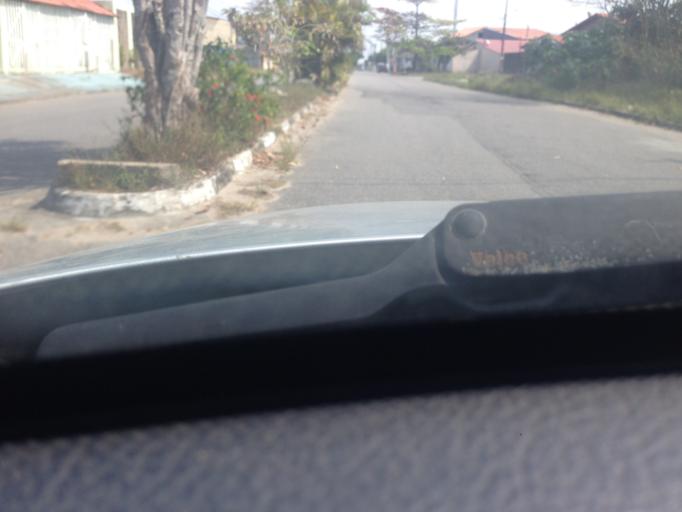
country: BR
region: Sao Paulo
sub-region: Itanhaem
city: Itanhaem
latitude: -24.2333
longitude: -46.8791
